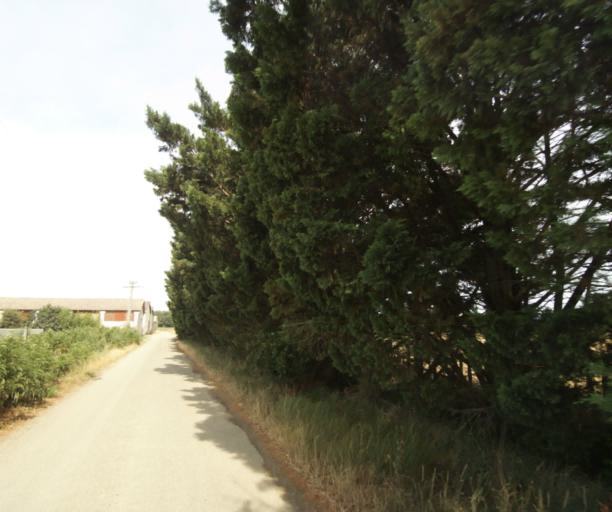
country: FR
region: Languedoc-Roussillon
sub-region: Departement de l'Herault
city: Marsillargues
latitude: 43.6329
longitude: 4.1829
